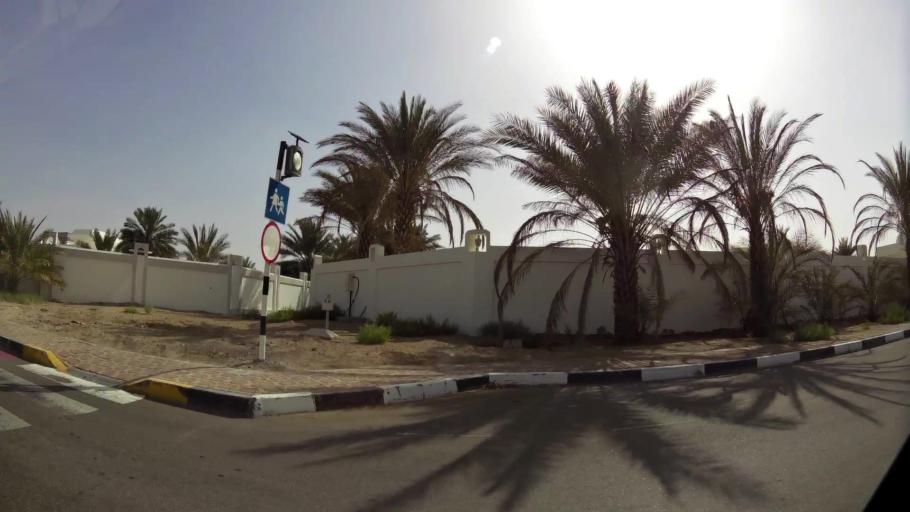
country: AE
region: Abu Dhabi
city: Al Ain
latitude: 24.2433
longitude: 55.6856
